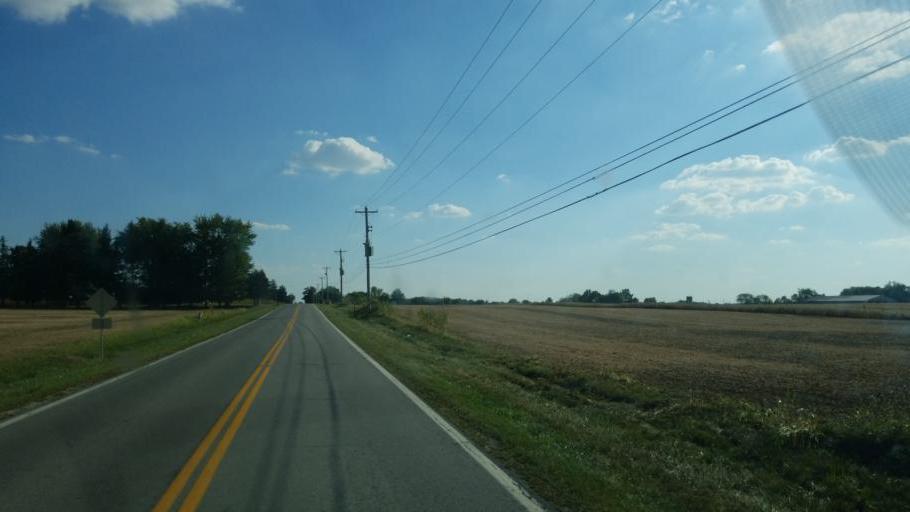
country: US
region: Ohio
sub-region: Union County
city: Richwood
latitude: 40.6058
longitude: -83.3805
